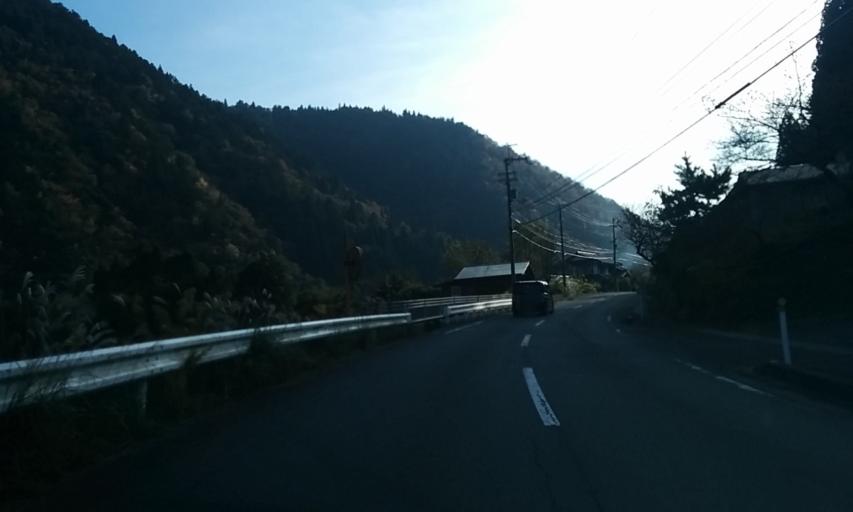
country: JP
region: Fukui
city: Obama
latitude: 35.2891
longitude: 135.5998
